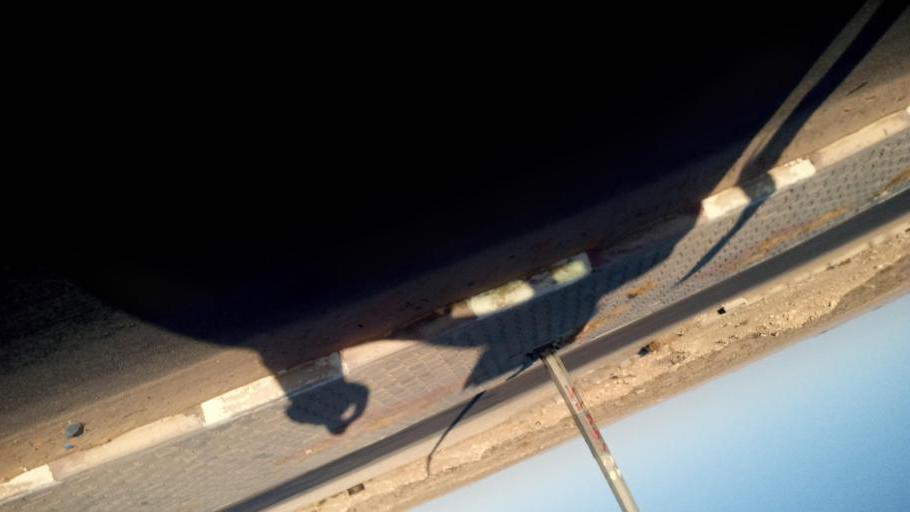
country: TN
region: Tataouine
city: Remada
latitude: 32.3636
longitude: 10.3180
